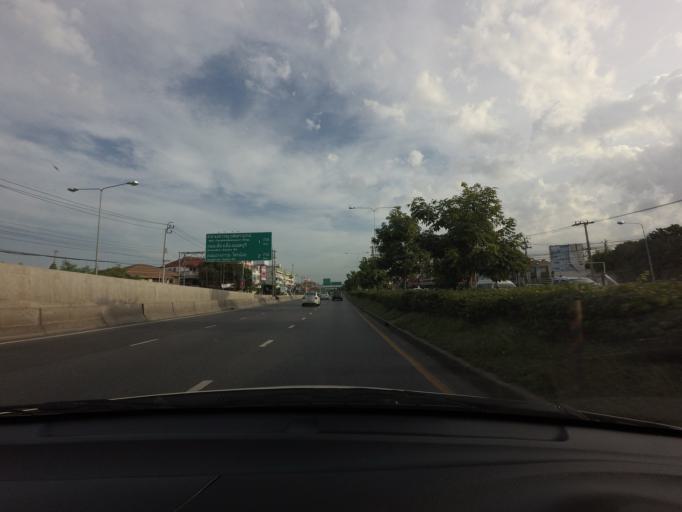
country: TH
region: Nonthaburi
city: Bang Kruai
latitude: 13.8561
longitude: 100.4501
